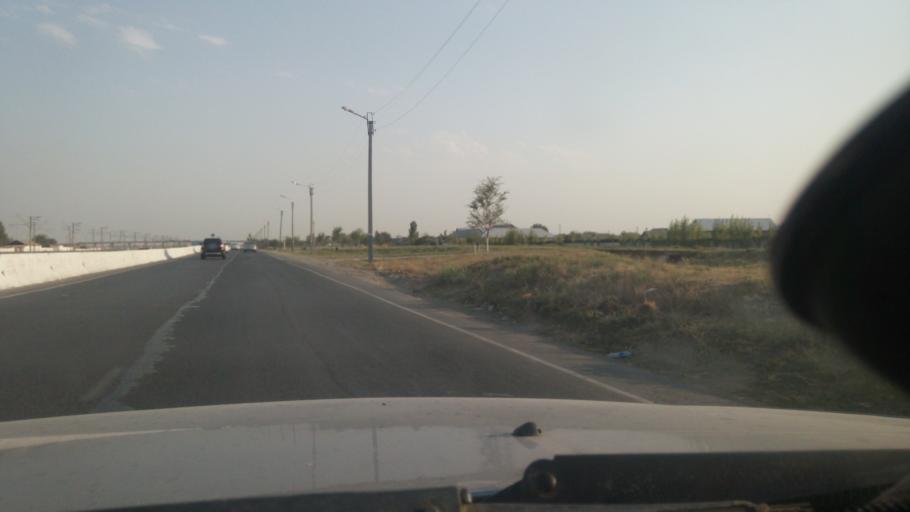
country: UZ
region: Sirdaryo
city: Guliston
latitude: 40.4827
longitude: 68.7681
